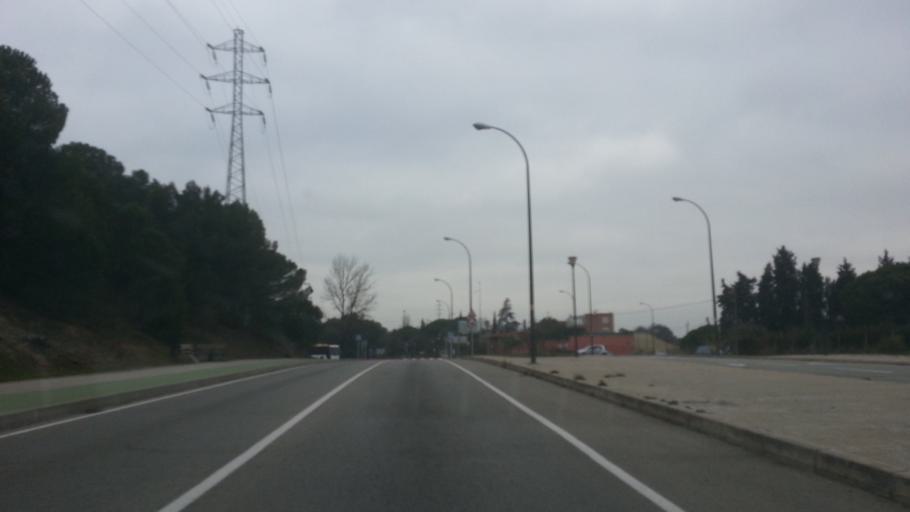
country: ES
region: Catalonia
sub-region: Provincia de Barcelona
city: Barbera del Valles
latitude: 41.5070
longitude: 2.1034
